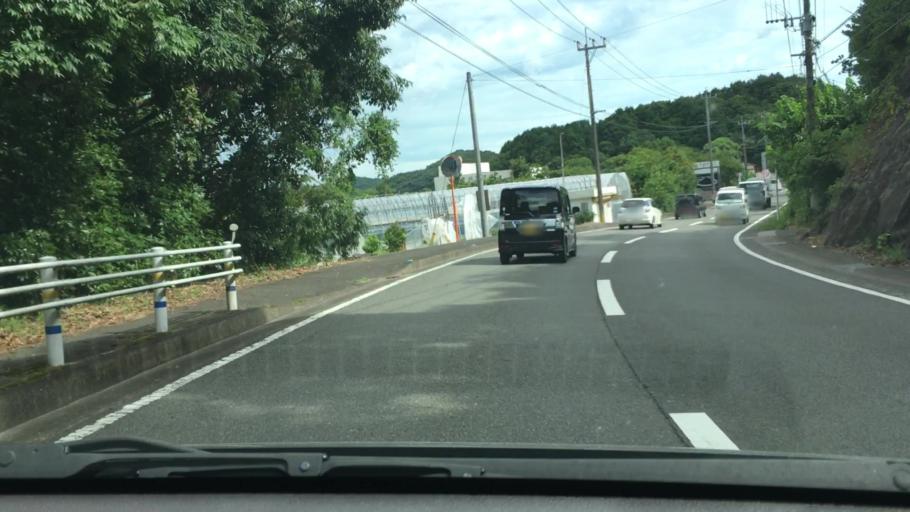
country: JP
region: Nagasaki
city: Togitsu
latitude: 32.9243
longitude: 129.7875
